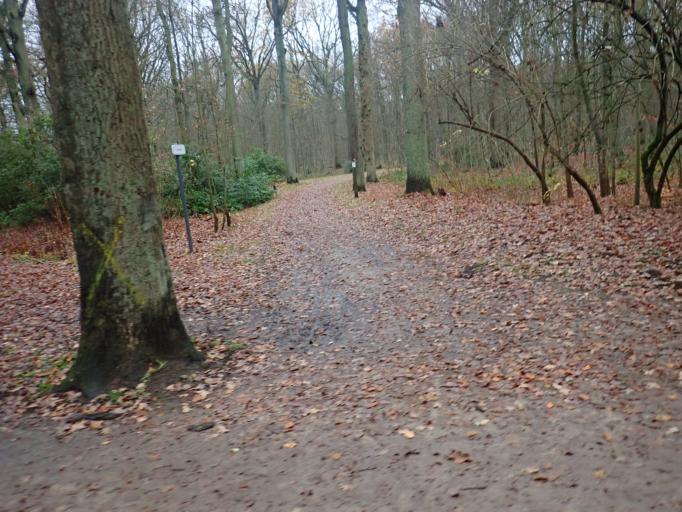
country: BE
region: Flanders
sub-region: Provincie Antwerpen
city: Brasschaat
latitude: 51.2810
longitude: 4.4930
